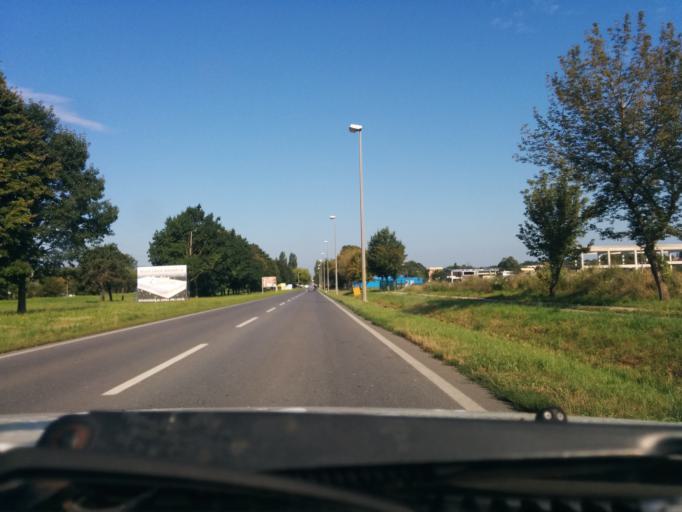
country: HR
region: Sisacko-Moslavacka
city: Kutina
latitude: 45.4756
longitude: 16.7860
